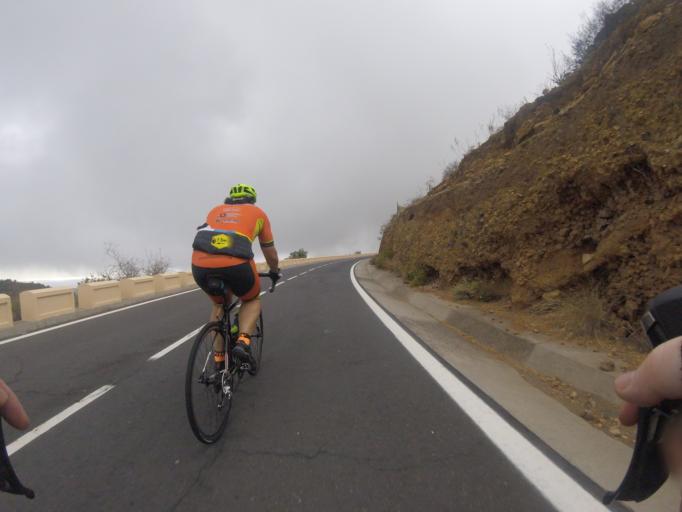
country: ES
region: Canary Islands
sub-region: Provincia de Santa Cruz de Tenerife
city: Lomo de Arico
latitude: 28.1886
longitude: -16.4801
